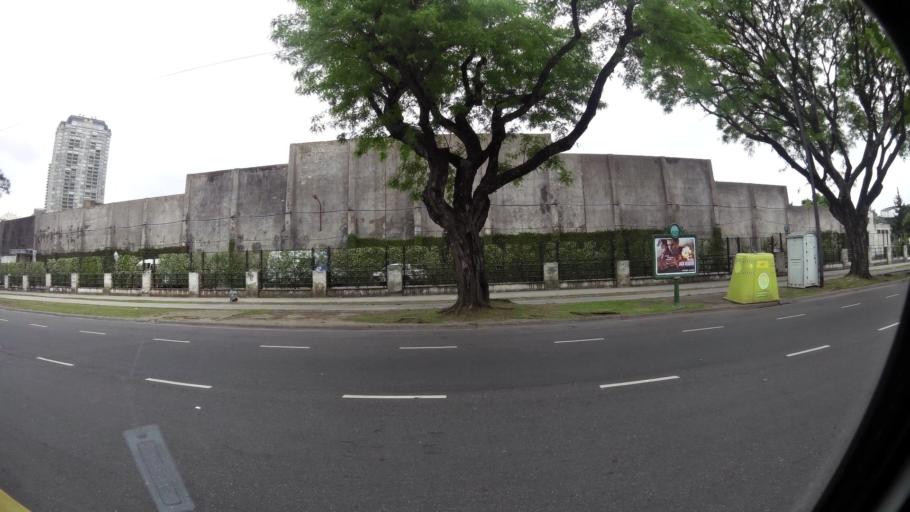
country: AR
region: Buenos Aires F.D.
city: Colegiales
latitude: -34.5468
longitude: -58.4525
